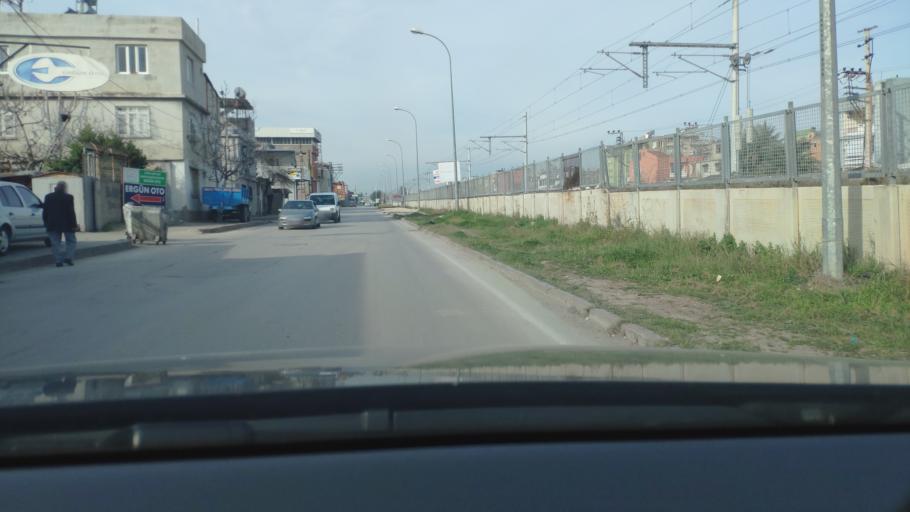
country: TR
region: Adana
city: Seyhan
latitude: 36.9976
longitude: 35.2710
